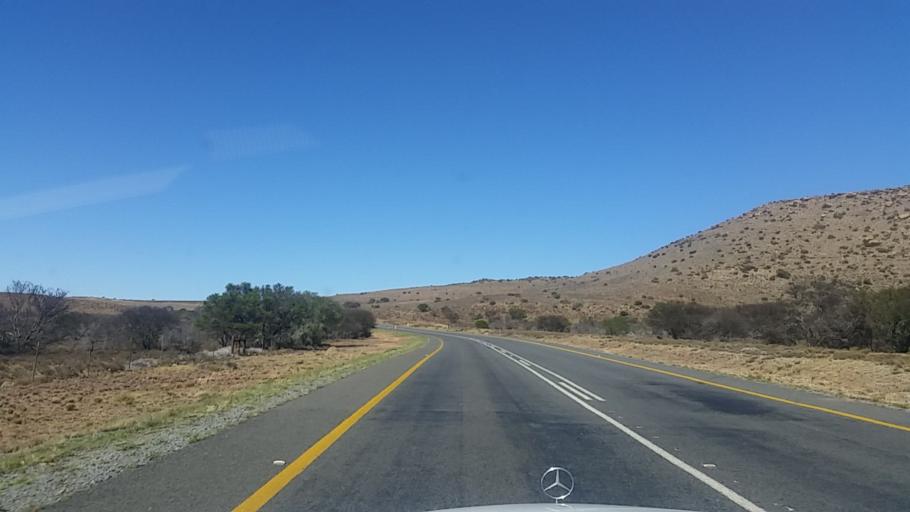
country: ZA
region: Eastern Cape
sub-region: Cacadu District Municipality
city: Graaff-Reinet
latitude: -31.9449
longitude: 24.7281
